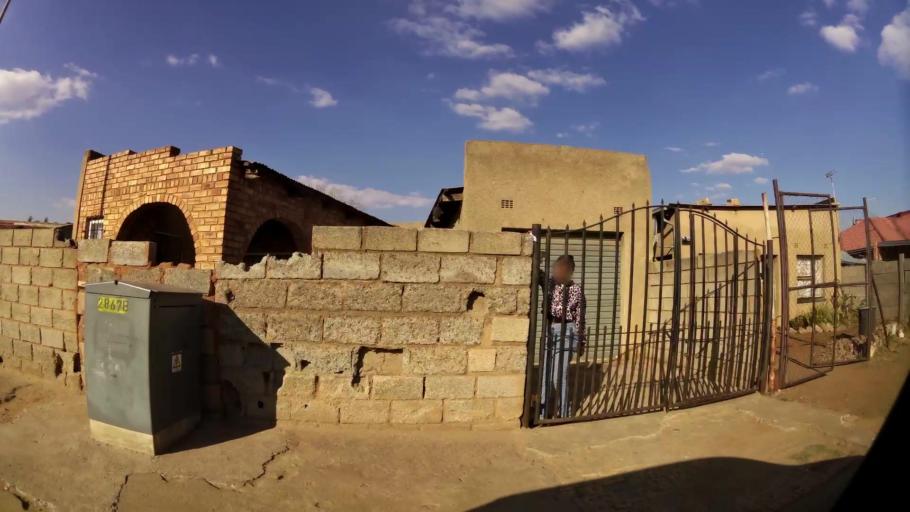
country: ZA
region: Gauteng
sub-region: City of Johannesburg Metropolitan Municipality
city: Soweto
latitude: -26.2184
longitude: 27.8760
